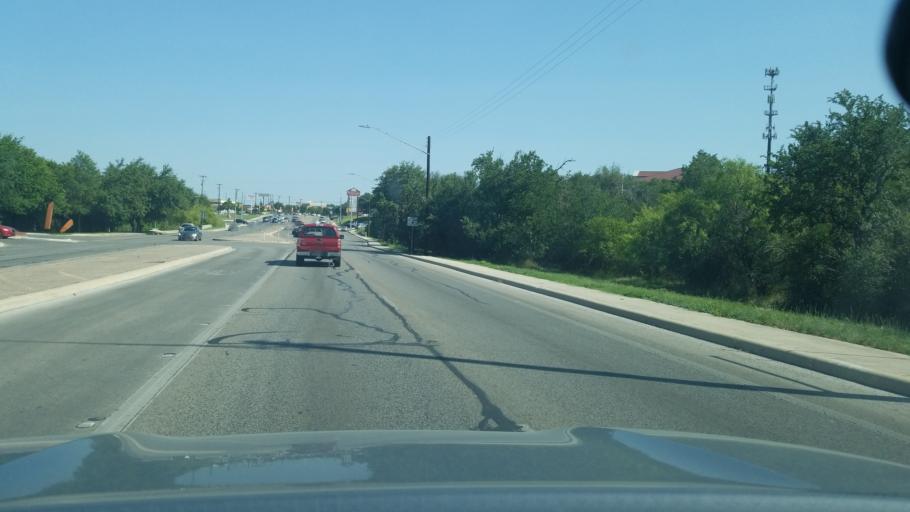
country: US
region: Texas
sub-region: Bexar County
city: Hollywood Park
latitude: 29.5812
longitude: -98.5154
